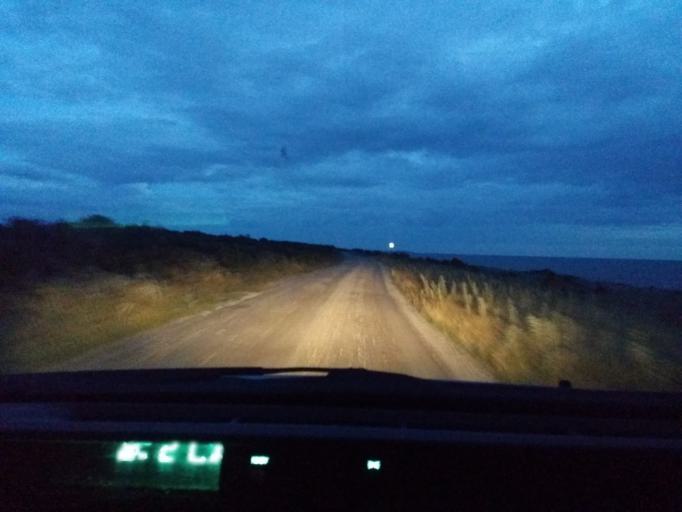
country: SE
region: Kalmar
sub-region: Borgholms Kommun
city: Borgholm
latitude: 57.1427
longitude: 16.9078
